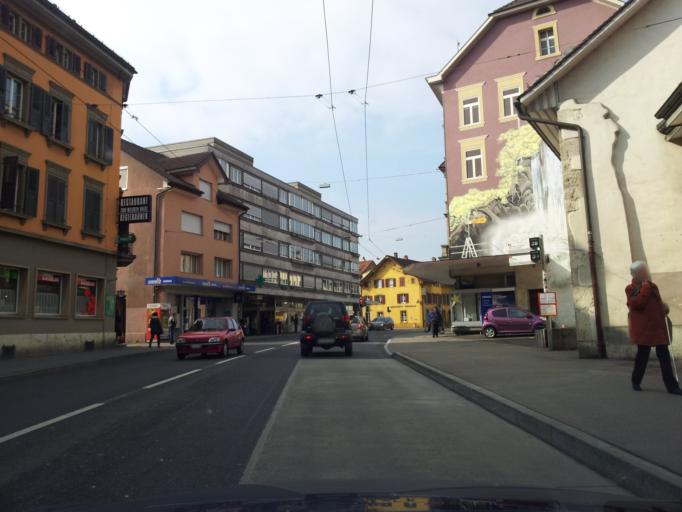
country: CH
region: Bern
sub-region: Biel/Bienne District
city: Biel/Bienne
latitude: 47.1530
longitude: 7.2672
